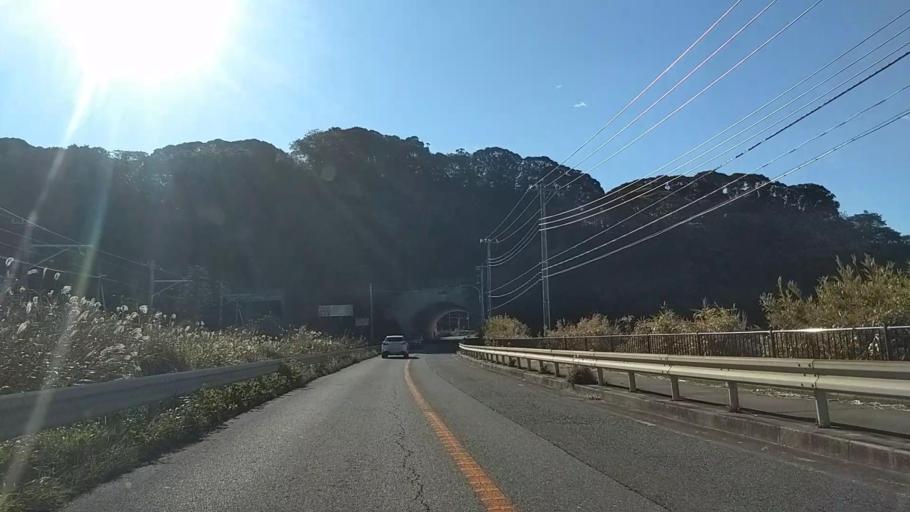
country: JP
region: Chiba
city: Futtsu
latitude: 35.1818
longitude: 139.8192
